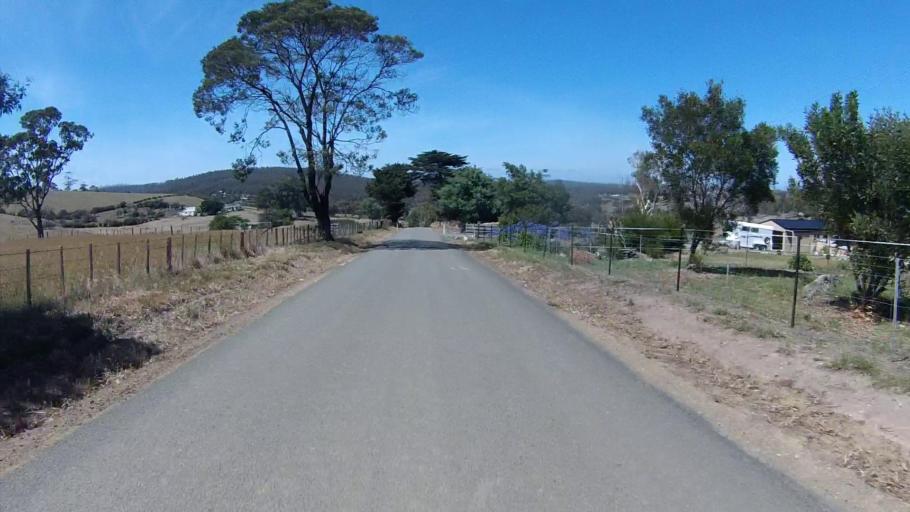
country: AU
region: Tasmania
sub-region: Sorell
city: Sorell
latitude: -42.7942
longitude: 147.6397
